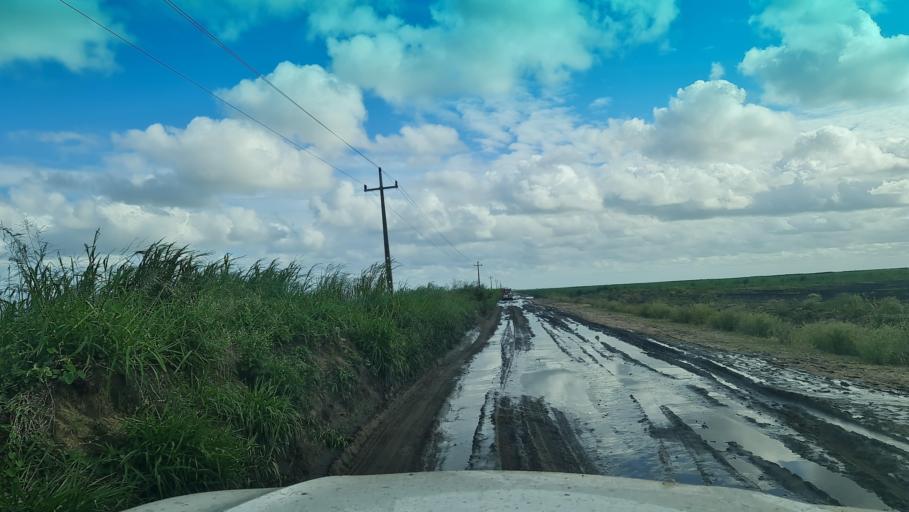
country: MZ
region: Maputo
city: Manhica
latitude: -25.4404
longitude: 32.8404
